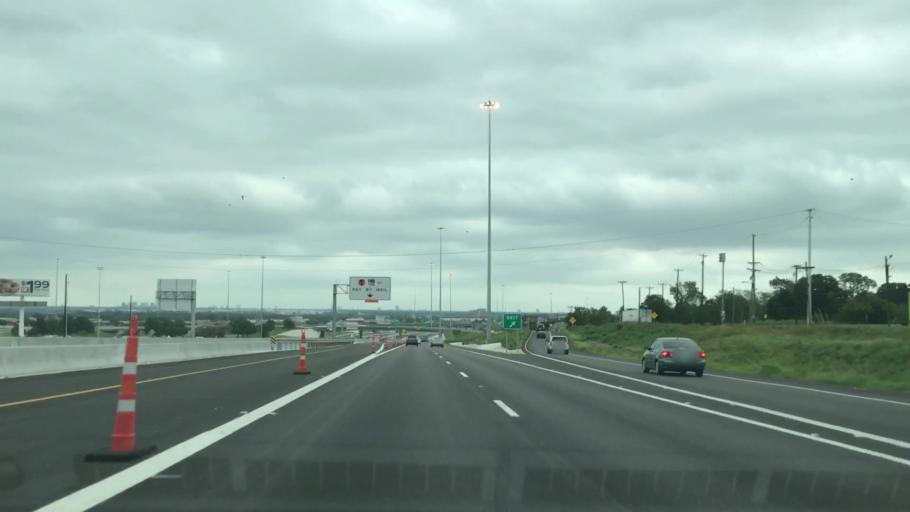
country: US
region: Texas
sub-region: Dallas County
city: Irving
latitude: 32.8369
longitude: -96.9133
